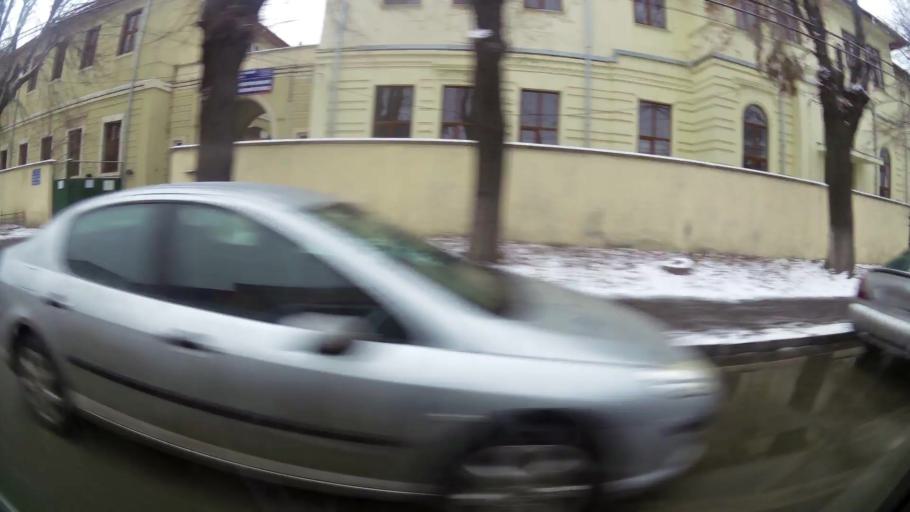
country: RO
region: Prahova
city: Ploiesti
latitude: 44.9388
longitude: 26.0305
